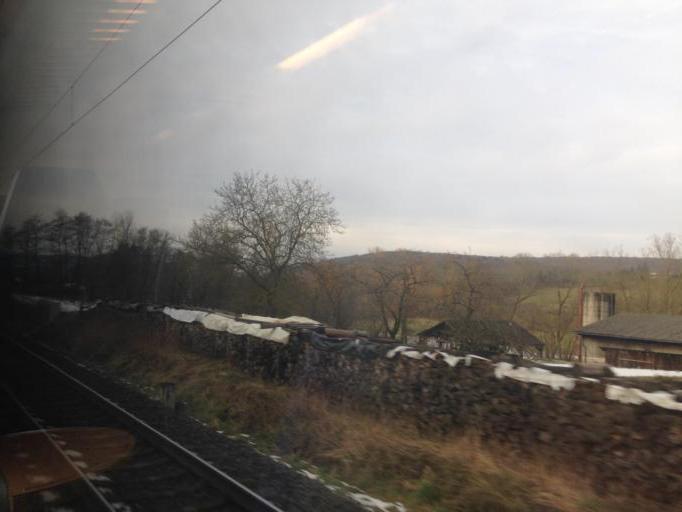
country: DE
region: Hesse
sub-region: Regierungsbezirk Giessen
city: Sinn
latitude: 50.6218
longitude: 8.3338
